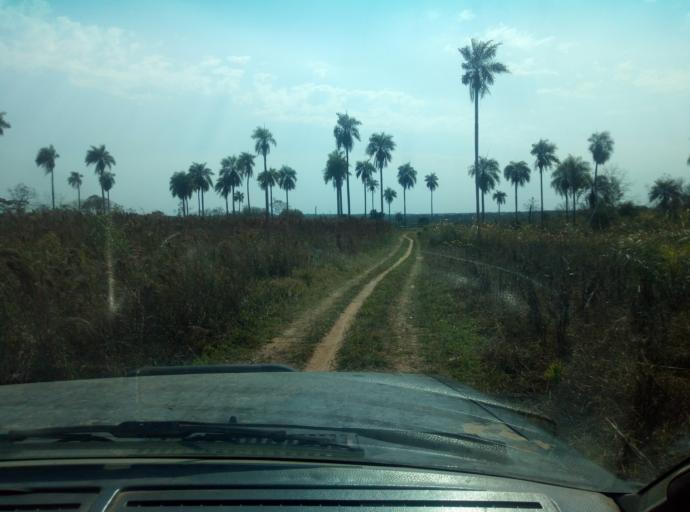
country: PY
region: Caaguazu
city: Doctor Cecilio Baez
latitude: -25.1366
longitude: -56.2416
